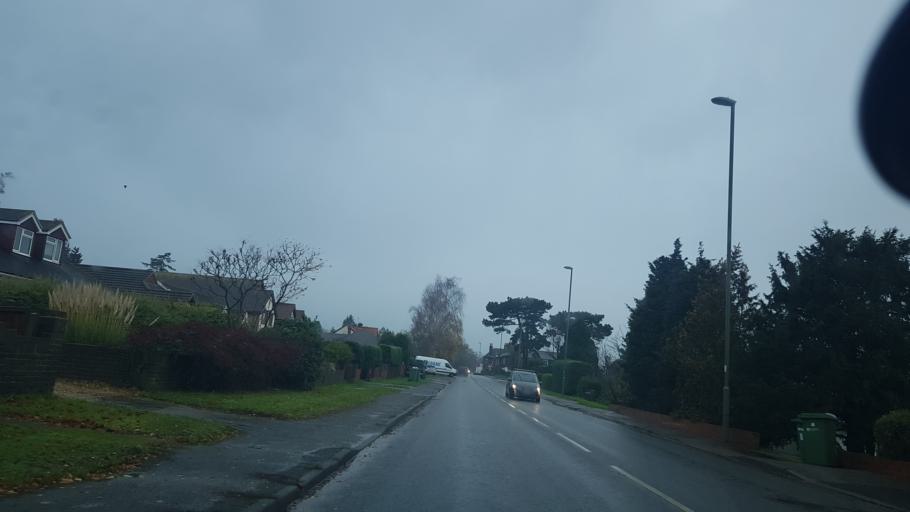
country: GB
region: England
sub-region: Surrey
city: Great Bookham
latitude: 51.2790
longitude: -0.3616
